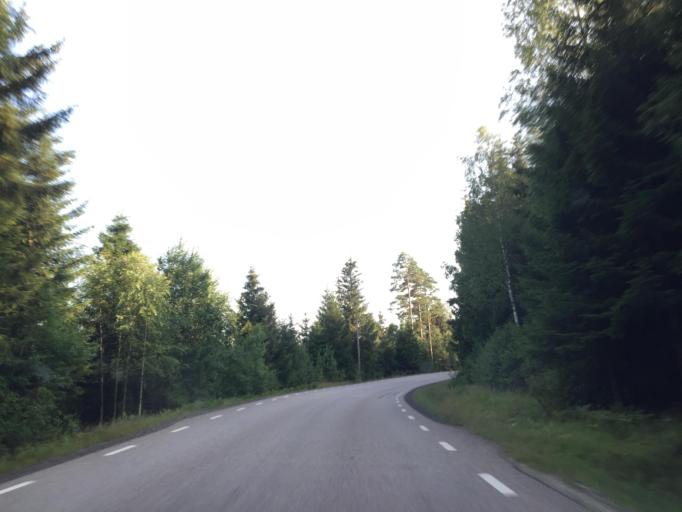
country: SE
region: Vaestra Goetaland
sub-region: Lilla Edets Kommun
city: Lilla Edet
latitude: 58.1358
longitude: 12.0091
